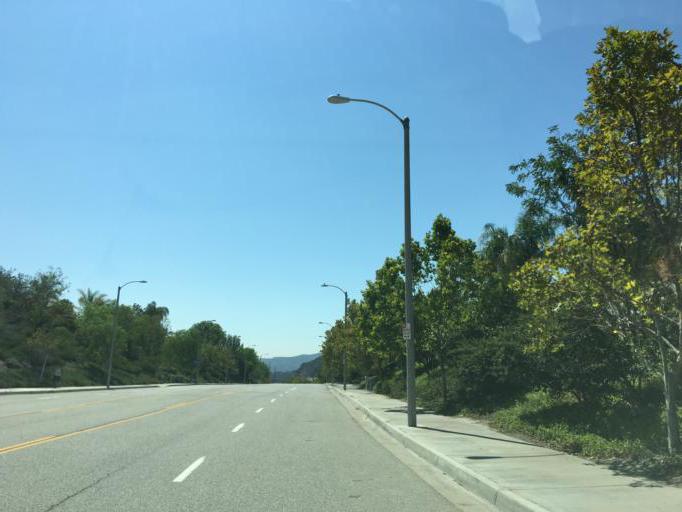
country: US
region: California
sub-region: Los Angeles County
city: Valencia
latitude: 34.3913
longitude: -118.6036
